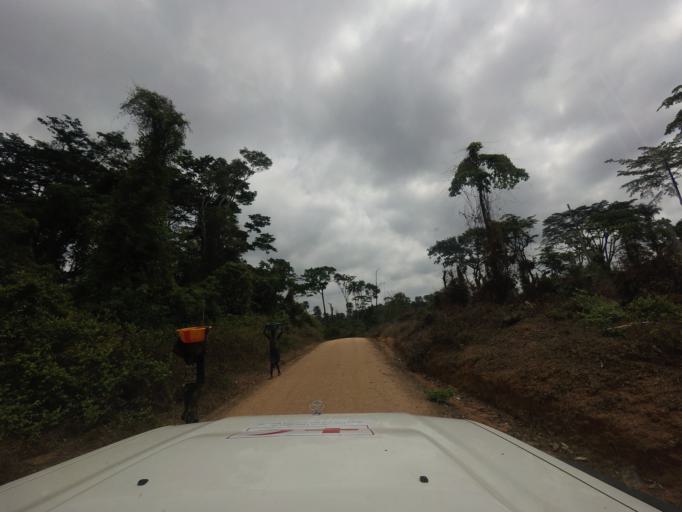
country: LR
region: Lofa
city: Voinjama
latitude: 8.4091
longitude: -9.7141
